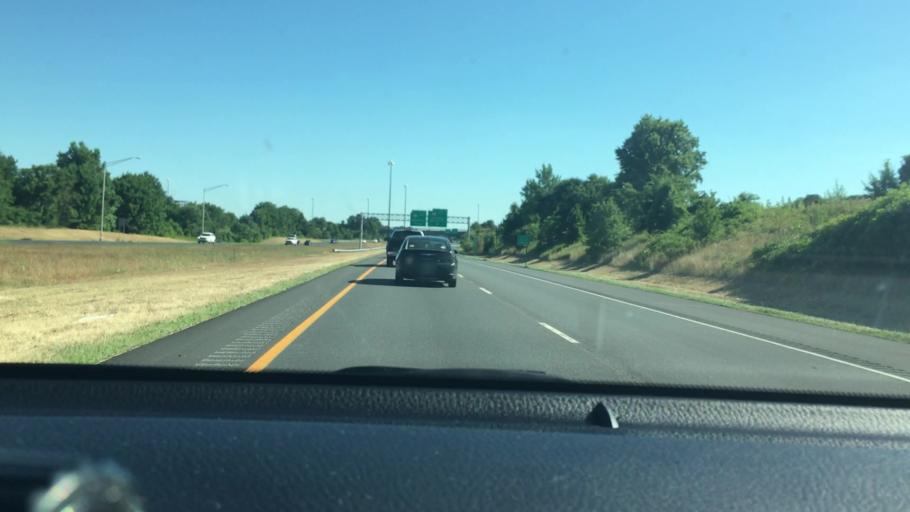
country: US
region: New Jersey
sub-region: Gloucester County
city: Richwood
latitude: 39.7252
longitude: -75.1526
